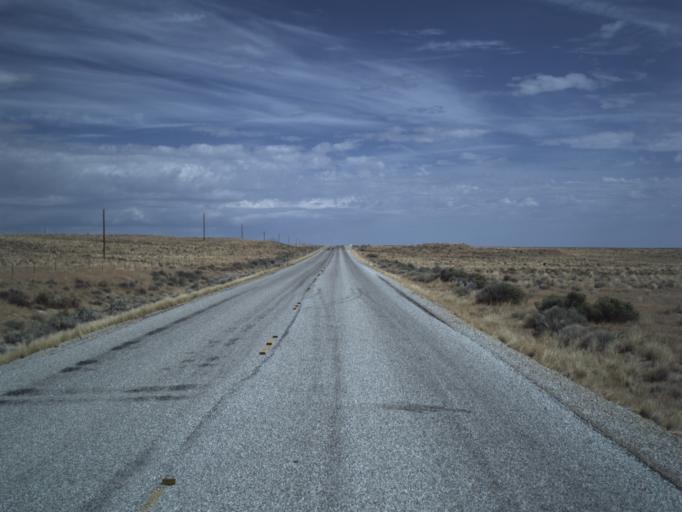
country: US
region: Utah
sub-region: Tooele County
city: Wendover
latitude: 41.4701
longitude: -113.6413
